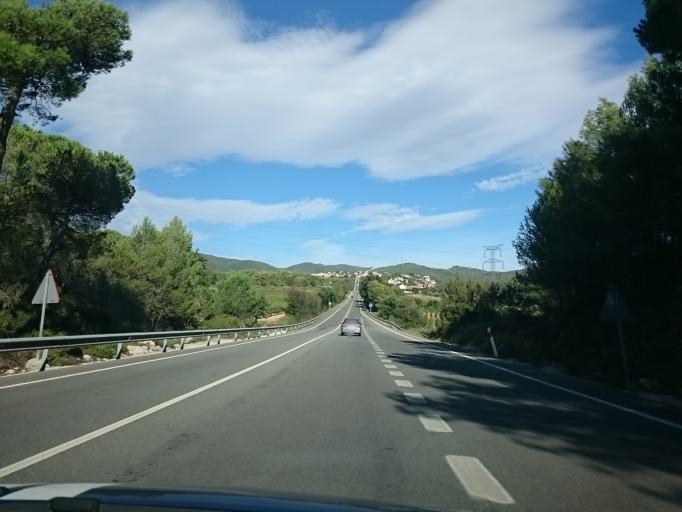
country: ES
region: Catalonia
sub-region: Provincia de Barcelona
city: Subirats
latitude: 41.3909
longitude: 1.8293
